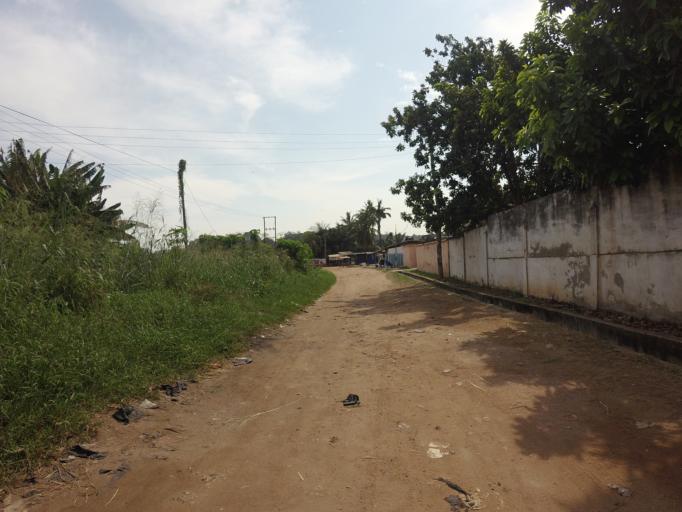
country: GH
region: Greater Accra
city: Dome
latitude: 5.6267
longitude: -0.2317
